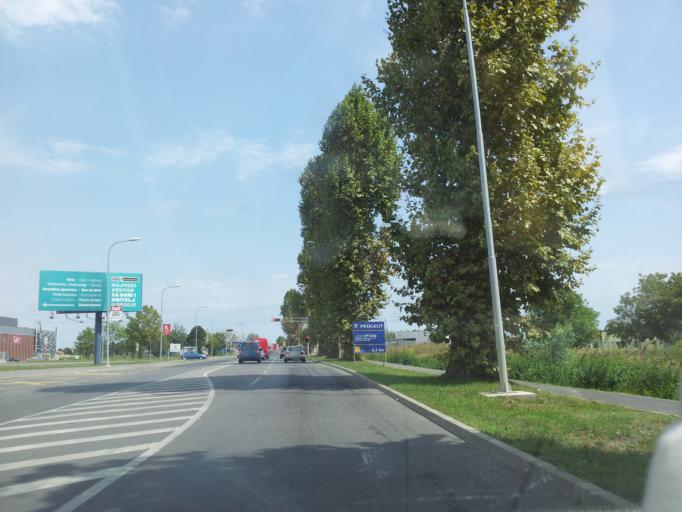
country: HR
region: Osjecko-Baranjska
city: Brijest
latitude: 45.5445
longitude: 18.6552
